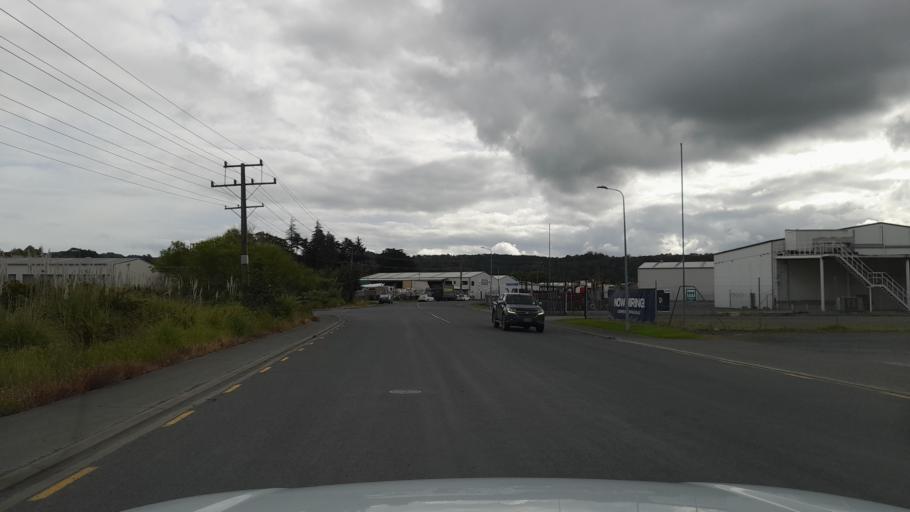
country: NZ
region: Northland
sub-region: Whangarei
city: Whangarei
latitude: -35.7486
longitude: 174.3133
